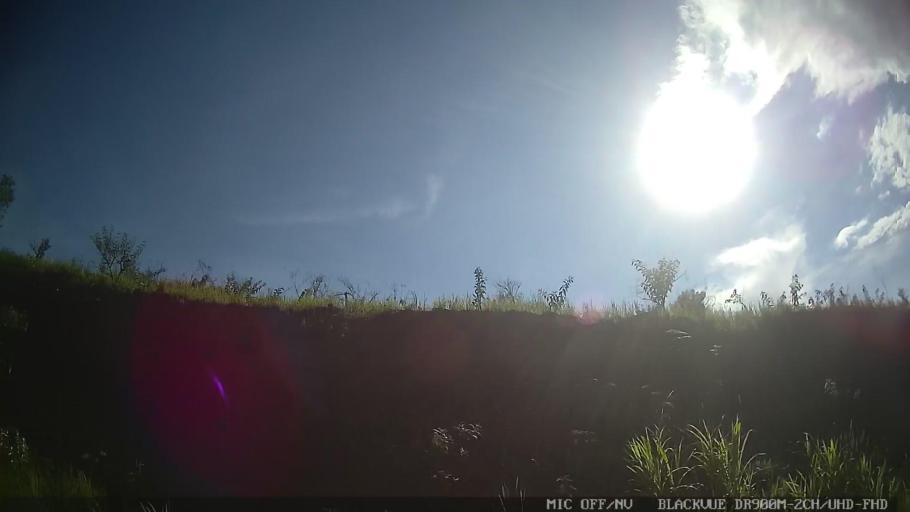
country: BR
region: Sao Paulo
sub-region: Serra Negra
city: Serra Negra
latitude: -22.6084
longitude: -46.7151
